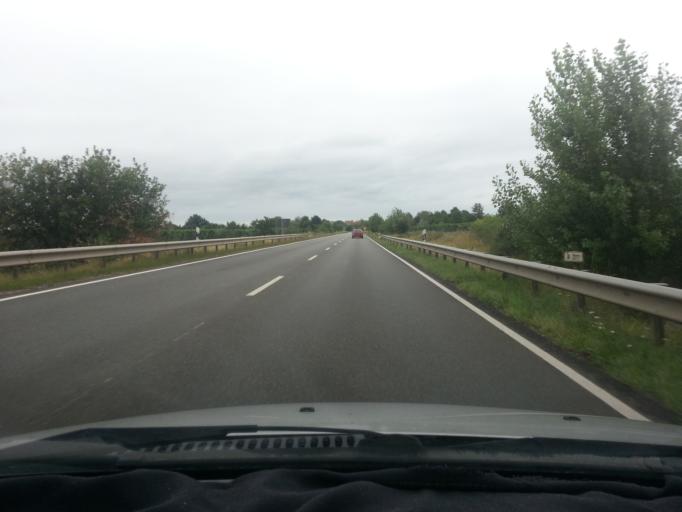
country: DE
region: Rheinland-Pfalz
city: Wachenheim
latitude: 49.4396
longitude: 8.2003
